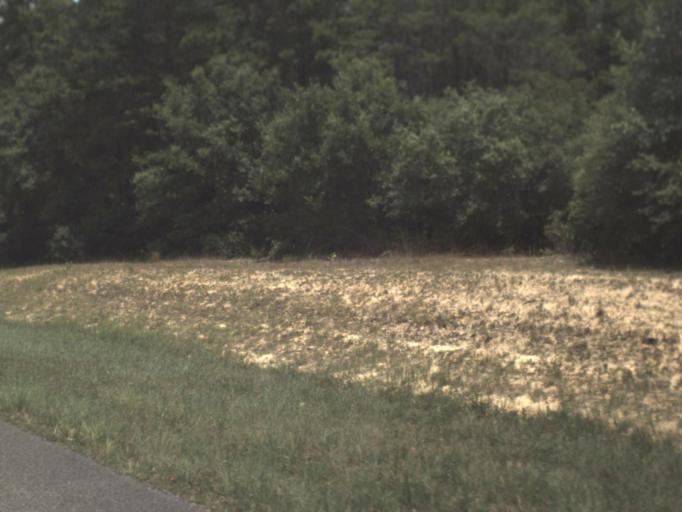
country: US
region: Florida
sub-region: Putnam County
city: Crescent City
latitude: 29.4429
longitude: -81.7378
